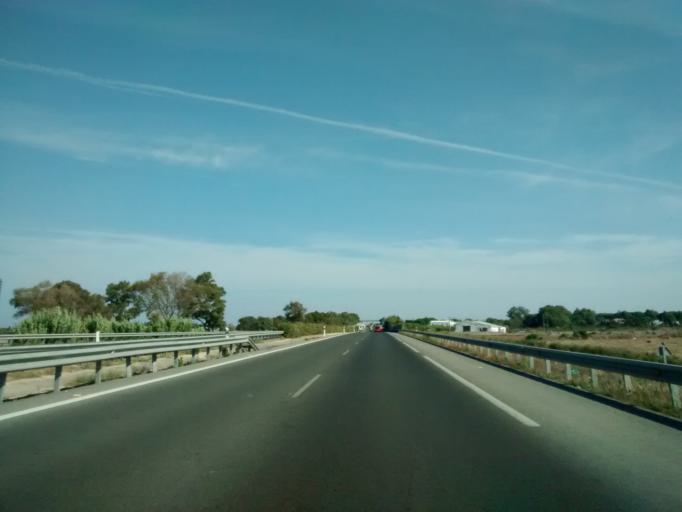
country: ES
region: Andalusia
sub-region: Provincia de Cadiz
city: Chiclana de la Frontera
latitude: 36.3698
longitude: -6.1128
